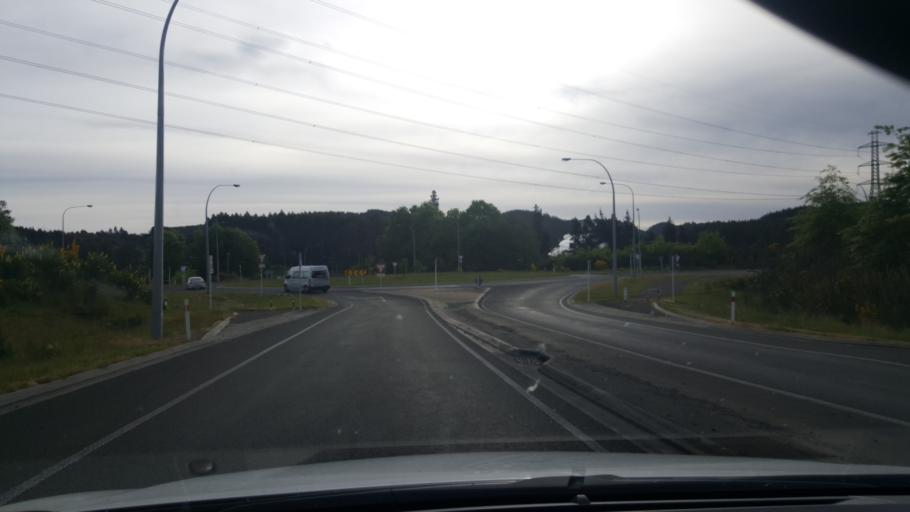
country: NZ
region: Waikato
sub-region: Taupo District
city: Taupo
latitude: -38.6232
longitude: 176.1010
